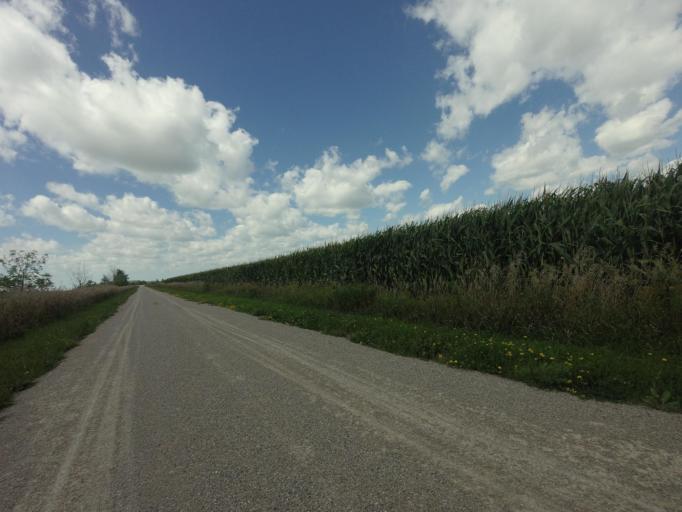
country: CA
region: Ontario
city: Huron East
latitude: 43.6062
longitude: -81.1202
